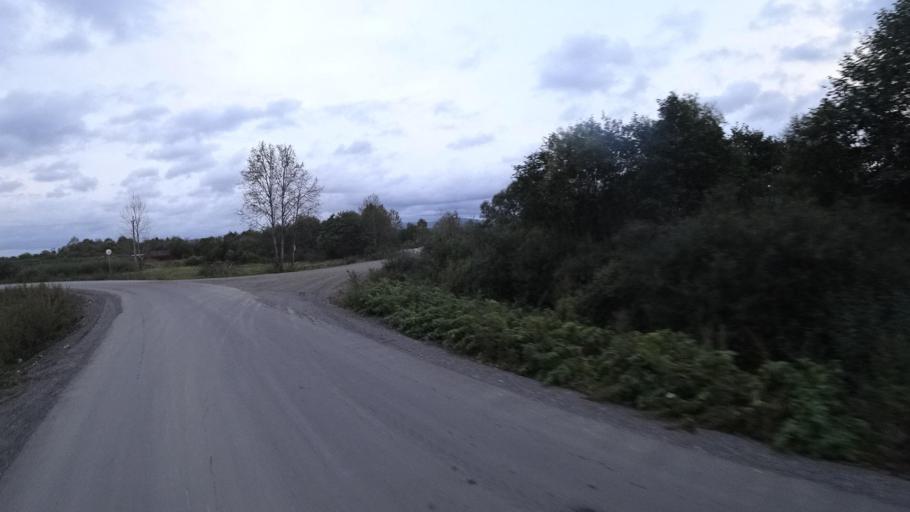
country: RU
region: Jewish Autonomous Oblast
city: Izvestkovyy
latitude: 48.9929
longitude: 131.5394
